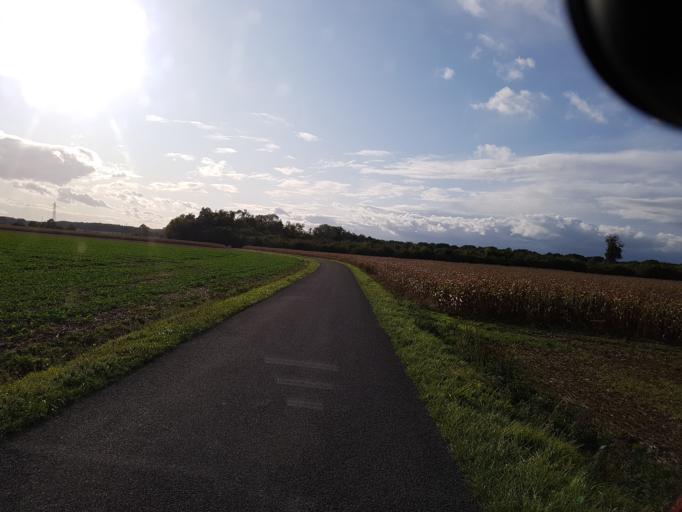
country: FR
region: Ile-de-France
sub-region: Departement de Seine-et-Marne
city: Touquin
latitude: 48.7500
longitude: 3.0244
